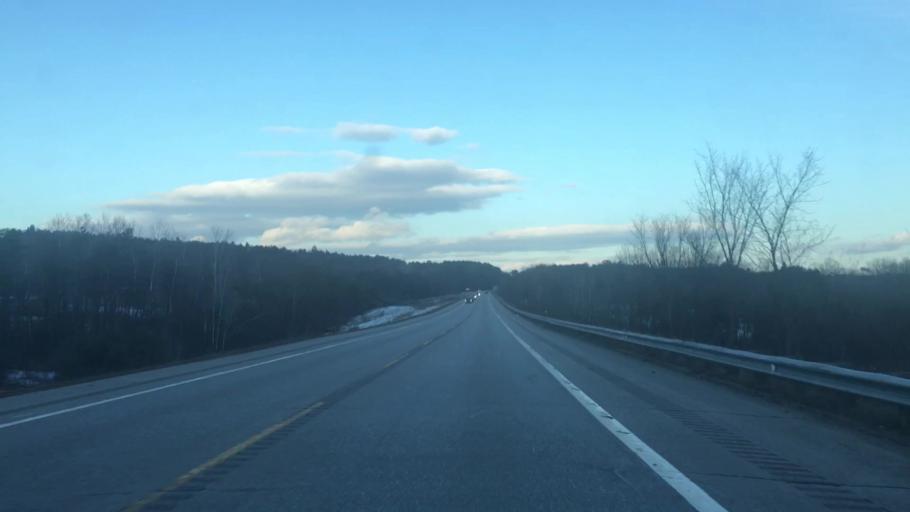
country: US
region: New Hampshire
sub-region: Merrimack County
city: Henniker
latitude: 43.1759
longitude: -71.8448
